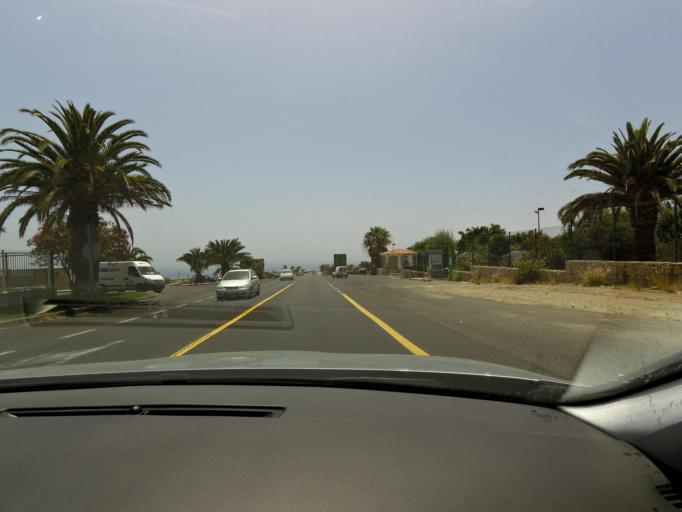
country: ES
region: Canary Islands
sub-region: Provincia de Santa Cruz de Tenerife
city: Adeje
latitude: 28.1272
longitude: -16.7451
